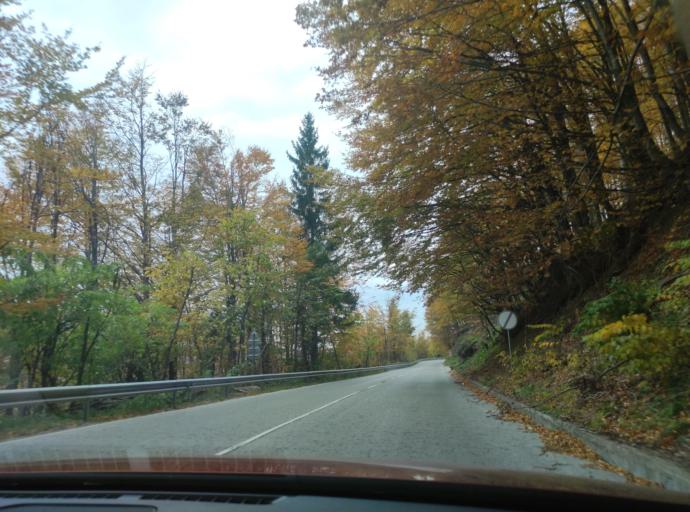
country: BG
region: Montana
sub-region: Obshtina Berkovitsa
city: Berkovitsa
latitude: 43.1450
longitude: 23.1436
